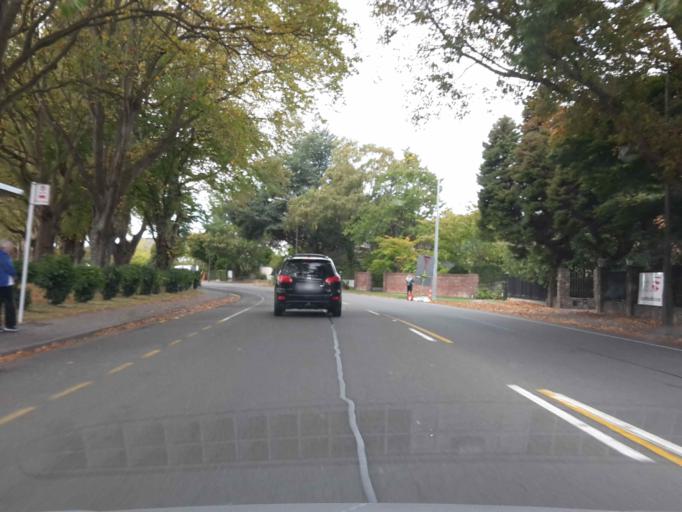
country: NZ
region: Canterbury
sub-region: Christchurch City
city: Christchurch
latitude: -43.5130
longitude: 172.6106
